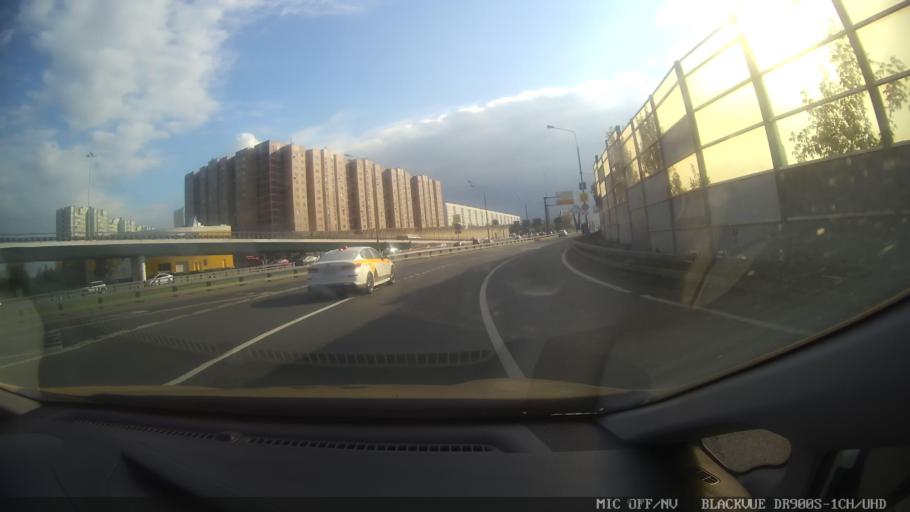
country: RU
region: Moscow
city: Yaroslavskiy
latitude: 55.8810
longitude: 37.7211
